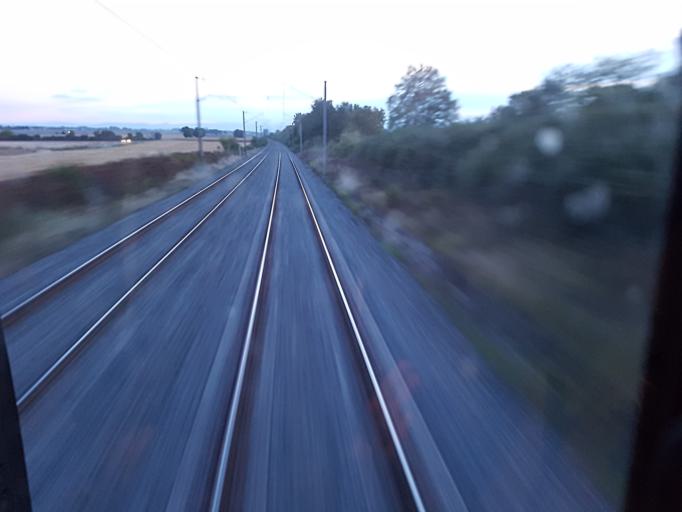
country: FR
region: Auvergne
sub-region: Departement du Puy-de-Dome
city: Ennezat
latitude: 45.9614
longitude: 3.2560
